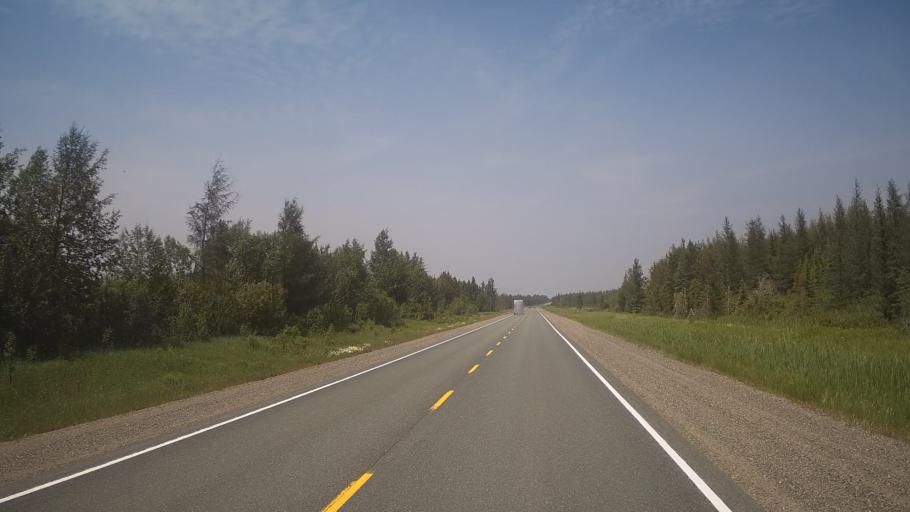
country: CA
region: Ontario
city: Timmins
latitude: 48.7585
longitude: -81.3603
